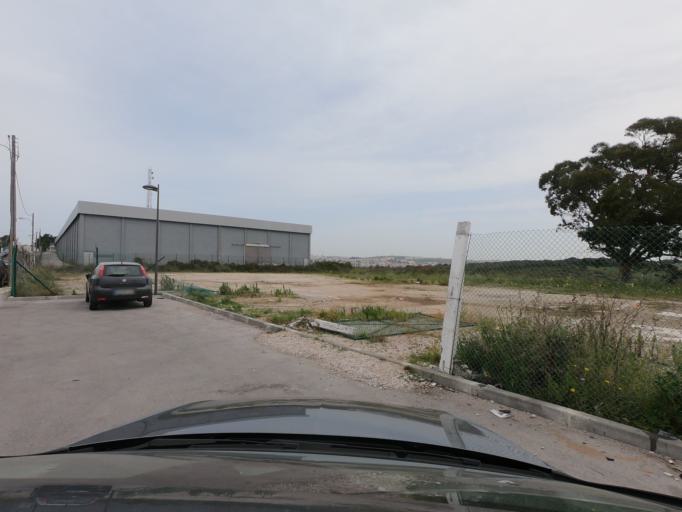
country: PT
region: Lisbon
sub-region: Oeiras
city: Barcarena
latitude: 38.7372
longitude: -9.2663
